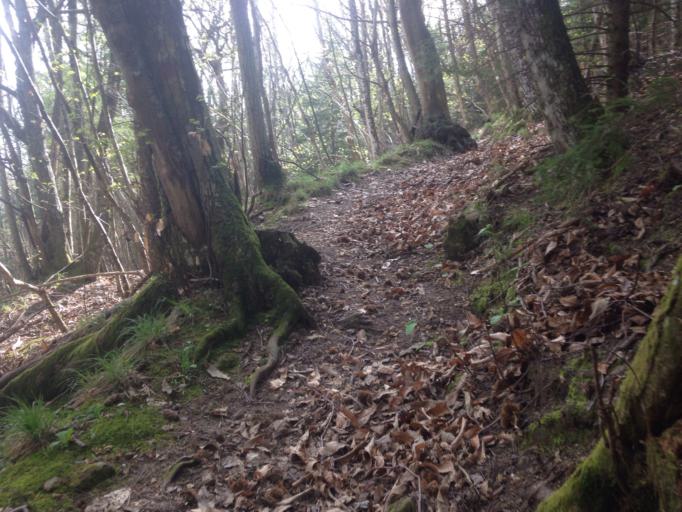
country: IT
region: Emilia-Romagna
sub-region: Provincia di Bologna
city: Lizzano in Belvedere
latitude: 44.1631
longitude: 10.8819
